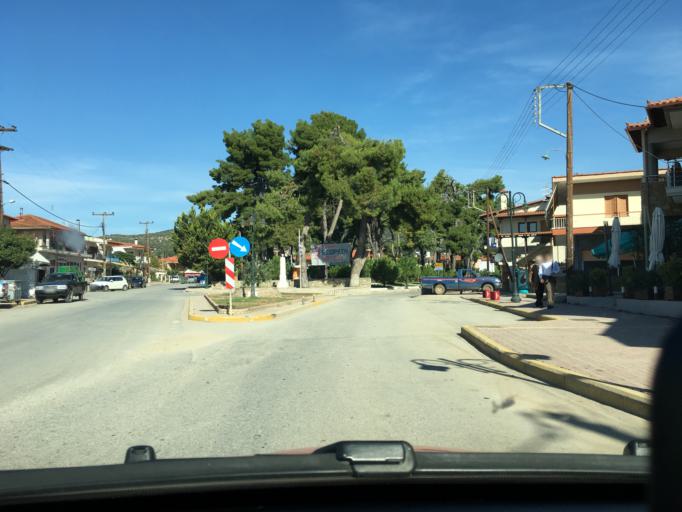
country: GR
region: Central Macedonia
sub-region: Nomos Chalkidikis
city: Ormylia
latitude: 40.2918
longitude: 23.5447
